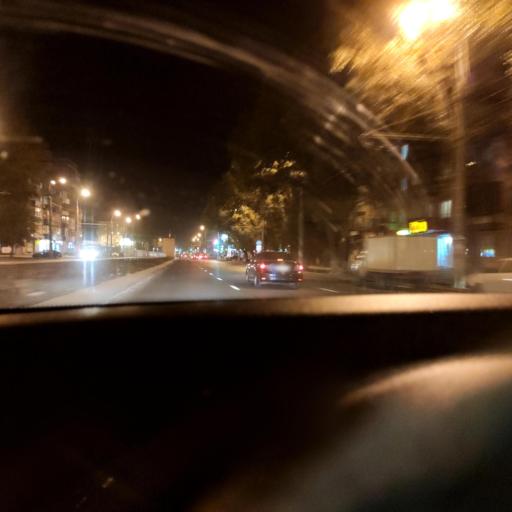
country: RU
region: Samara
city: Samara
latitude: 53.2054
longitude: 50.2324
